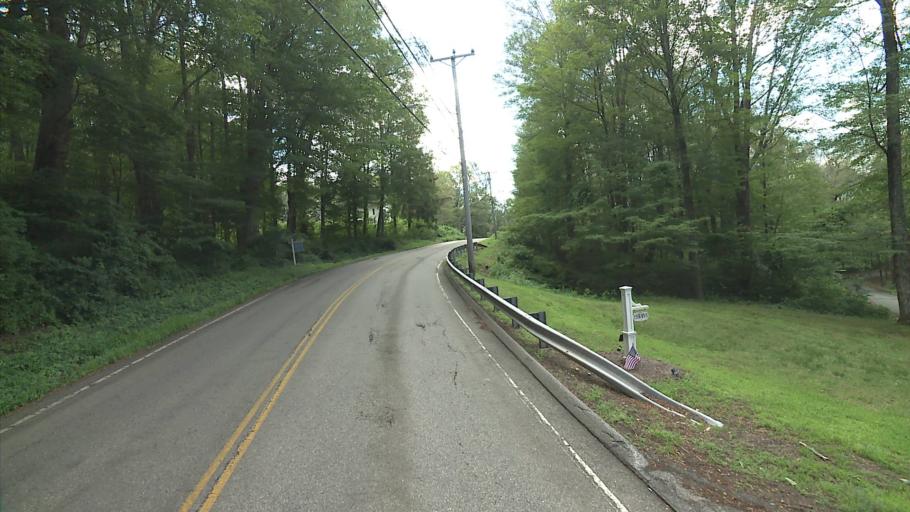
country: US
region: Connecticut
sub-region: Middlesex County
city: Higganum
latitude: 41.5430
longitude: -72.5450
